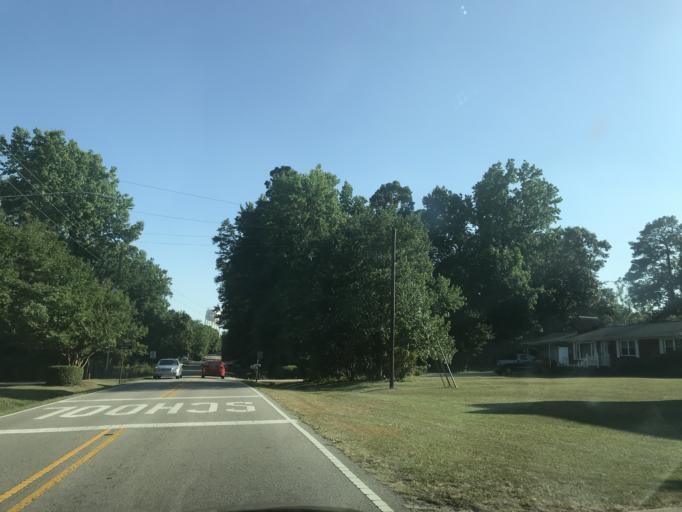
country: US
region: North Carolina
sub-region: Wake County
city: Garner
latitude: 35.7114
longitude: -78.6036
